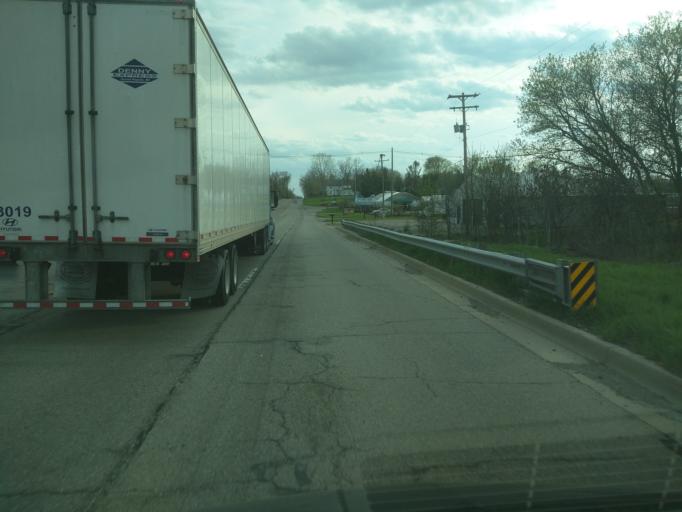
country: US
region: Michigan
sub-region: Eaton County
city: Eaton Rapids
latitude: 42.5261
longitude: -84.6452
